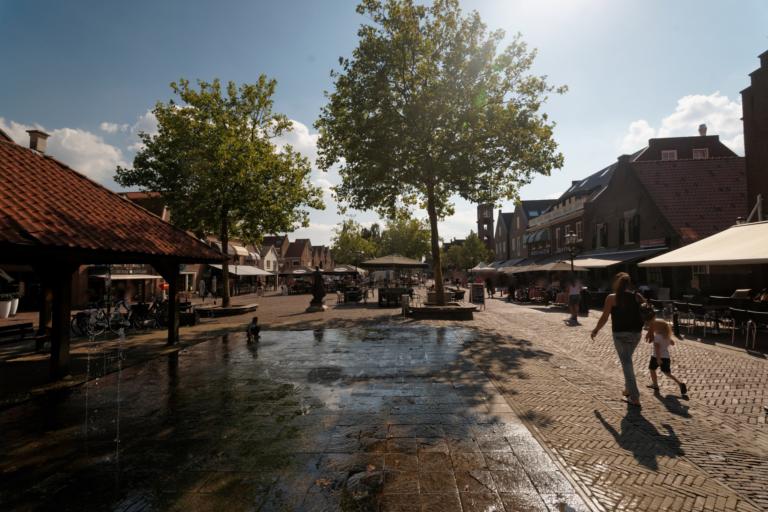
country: NL
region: Utrecht
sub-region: Gemeente Bunschoten
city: Bunschoten
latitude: 52.2533
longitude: 5.3779
